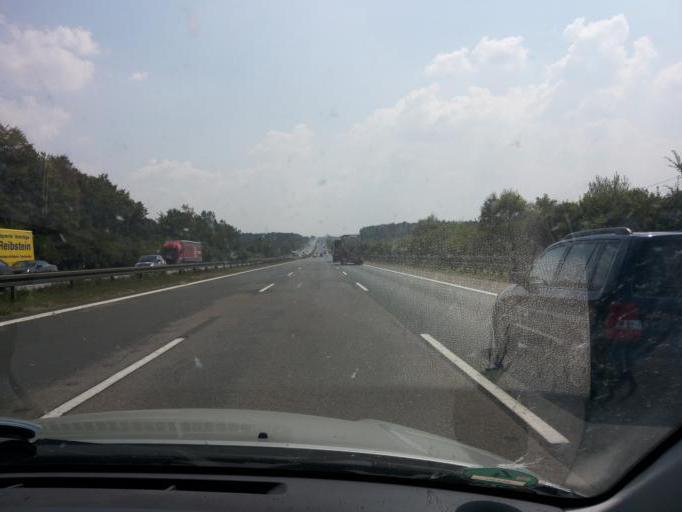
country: DE
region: Bavaria
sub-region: Regierungsbezirk Mittelfranken
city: Hilpoltstein
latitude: 49.1957
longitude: 11.2442
